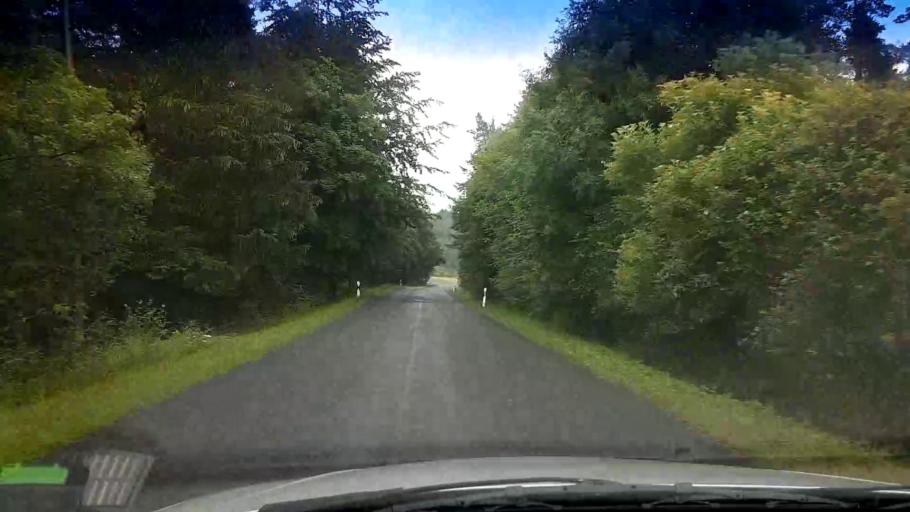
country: DE
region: Bavaria
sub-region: Upper Franconia
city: Altendorf
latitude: 50.0729
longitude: 11.1768
